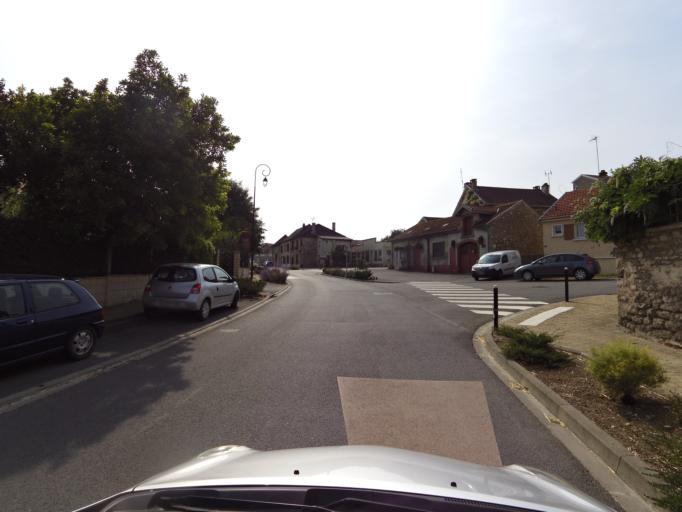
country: FR
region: Champagne-Ardenne
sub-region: Departement de la Marne
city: Gueux
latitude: 49.1754
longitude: 3.8634
